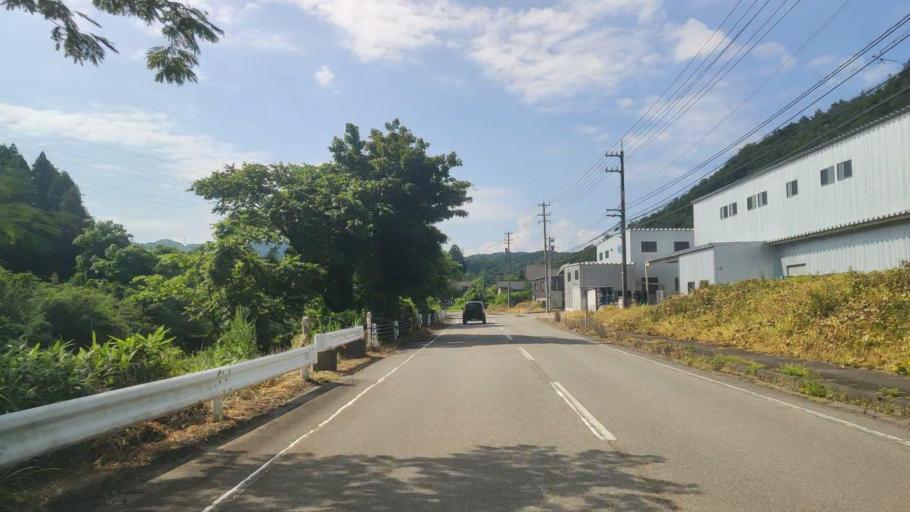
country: JP
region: Ishikawa
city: Komatsu
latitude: 36.3494
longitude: 136.5050
